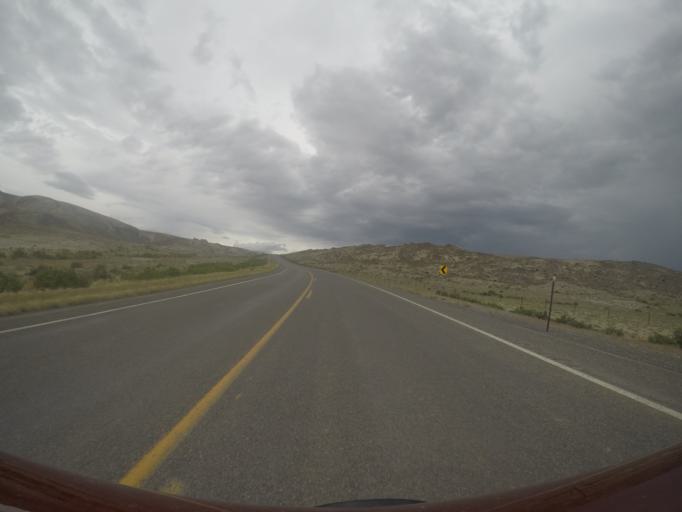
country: US
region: Wyoming
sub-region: Big Horn County
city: Lovell
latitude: 44.8804
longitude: -108.2897
